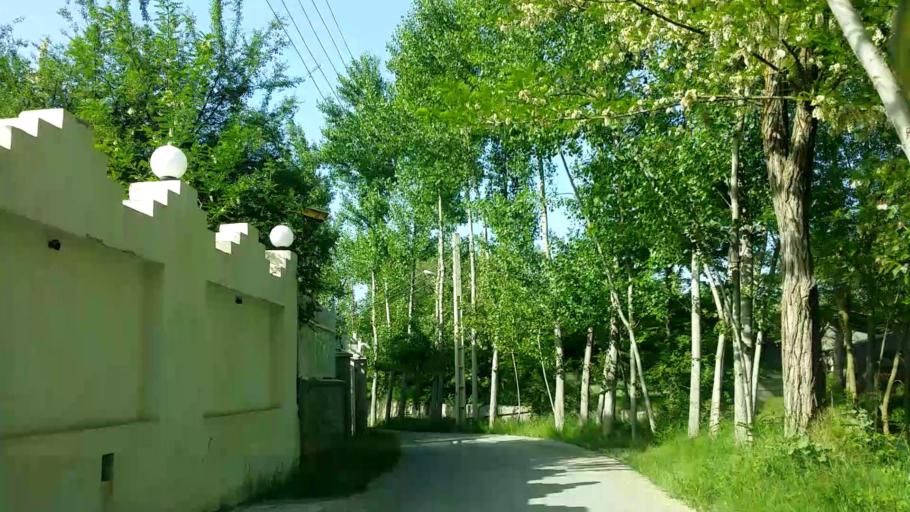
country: IR
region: Mazandaran
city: `Abbasabad
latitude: 36.5179
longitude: 51.1735
